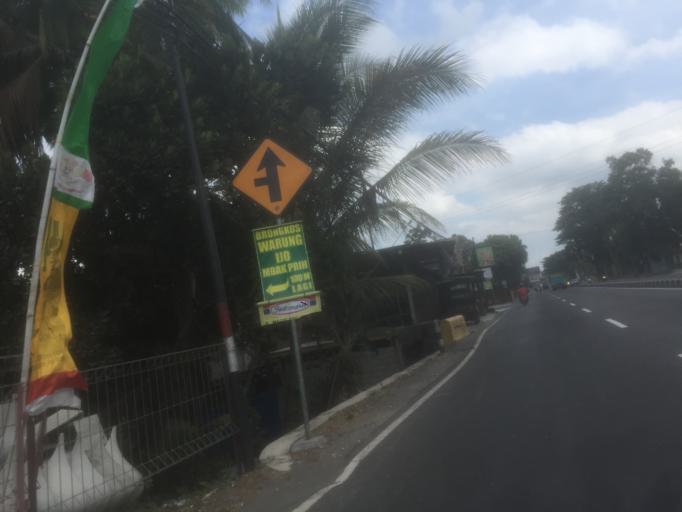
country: ID
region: Daerah Istimewa Yogyakarta
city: Sleman
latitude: -7.6609
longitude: 110.3283
